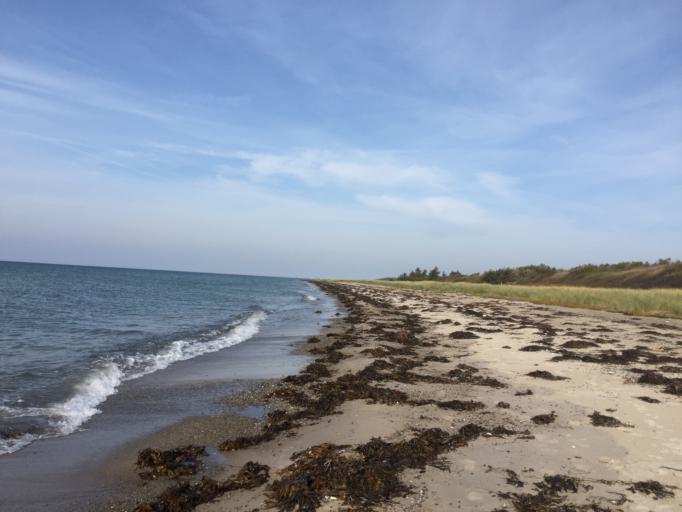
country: DK
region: Zealand
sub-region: Slagelse Kommune
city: Korsor
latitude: 55.2269
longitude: 11.1717
